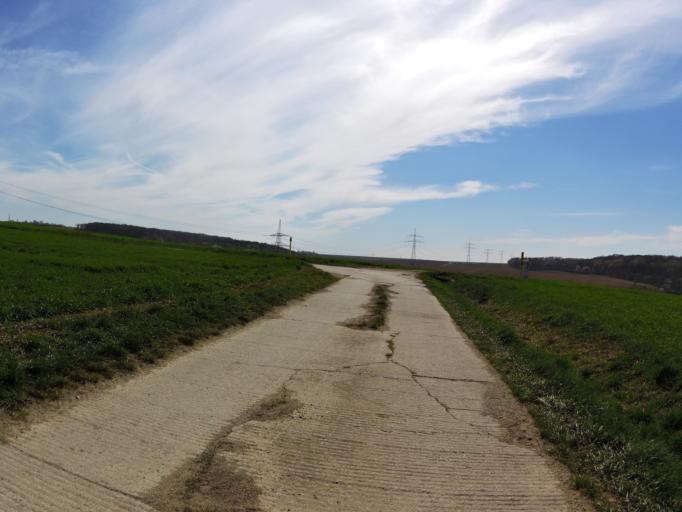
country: DE
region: Bavaria
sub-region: Regierungsbezirk Unterfranken
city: Rottendorf
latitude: 49.7872
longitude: 10.0430
